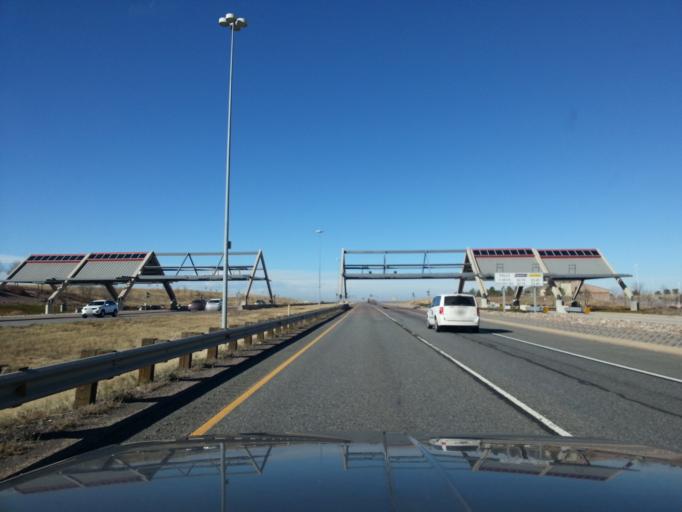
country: US
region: Colorado
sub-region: Adams County
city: Brighton
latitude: 39.8604
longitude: -104.7494
